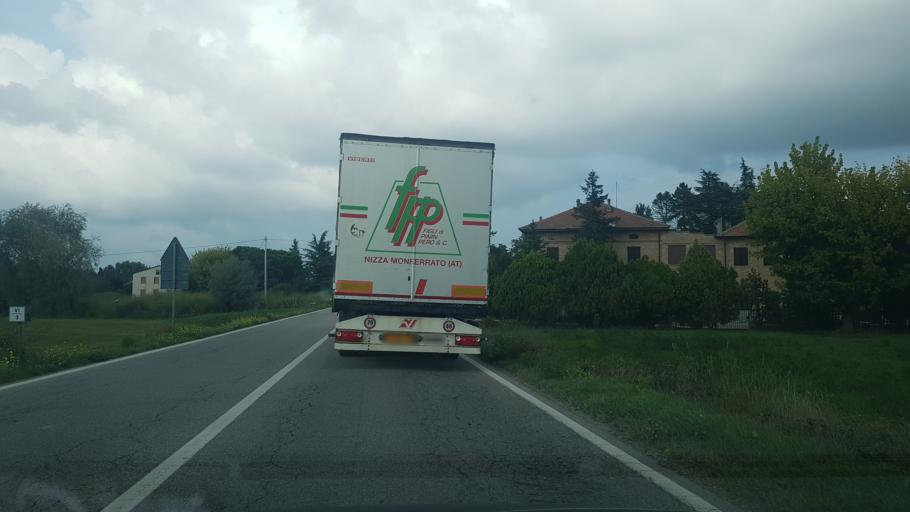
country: IT
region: Piedmont
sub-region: Provincia di Asti
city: Calamandrana
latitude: 44.7438
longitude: 8.3435
